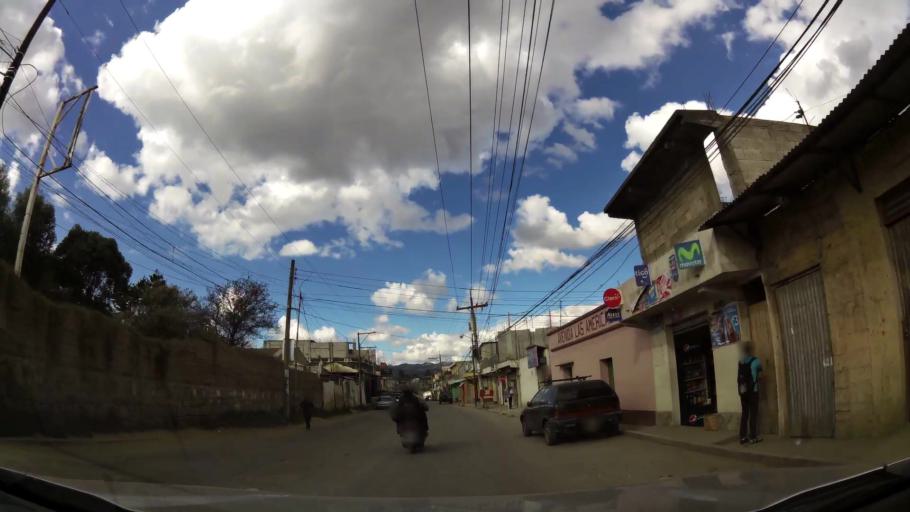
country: GT
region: Quetzaltenango
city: Quetzaltenango
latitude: 14.8374
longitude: -91.5356
